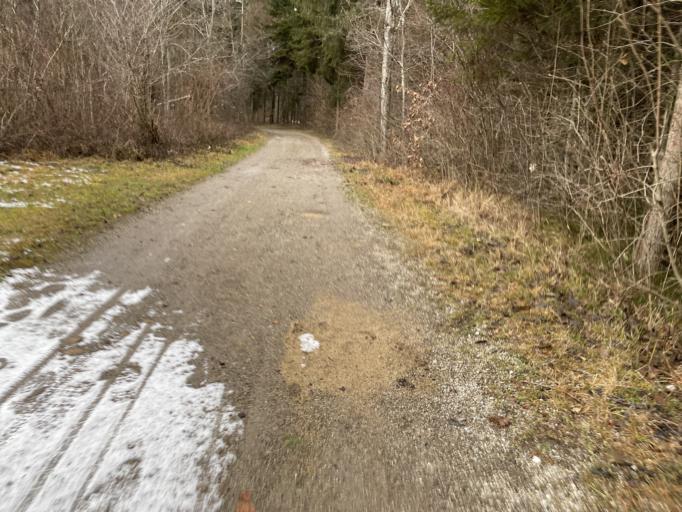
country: CH
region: Bern
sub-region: Bern-Mittelland District
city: Niederwichtrach
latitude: 46.8457
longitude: 7.5582
